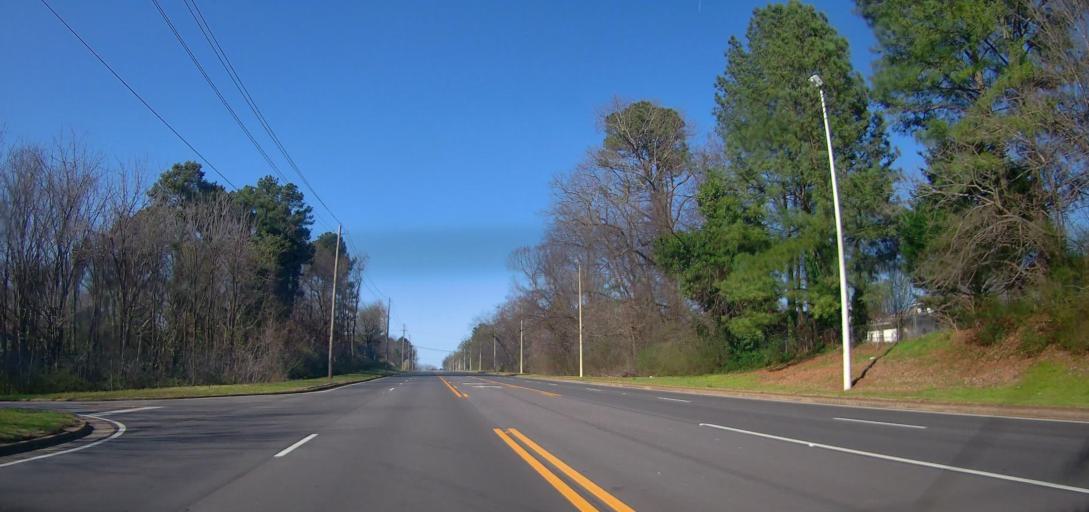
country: US
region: Alabama
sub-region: Lauderdale County
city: East Florence
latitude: 34.8166
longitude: -87.6266
